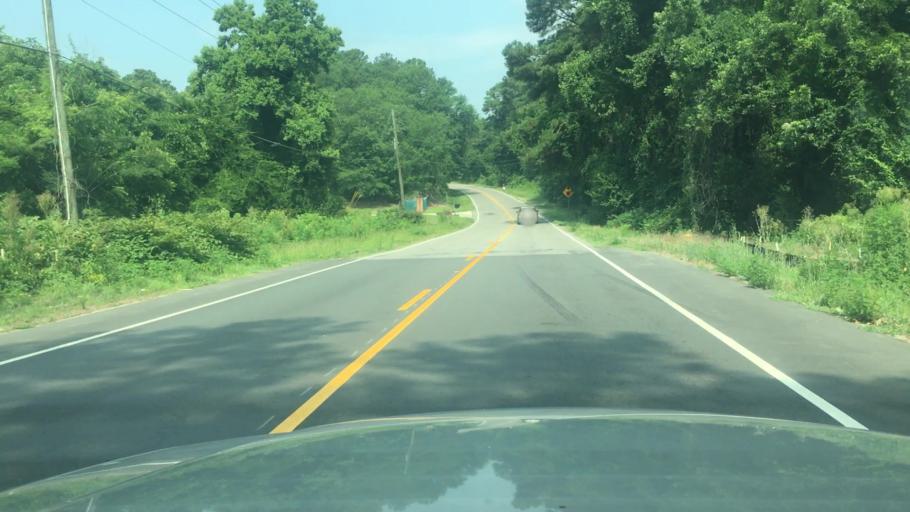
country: US
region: North Carolina
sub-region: Cumberland County
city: Hope Mills
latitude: 35.0020
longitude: -78.9606
